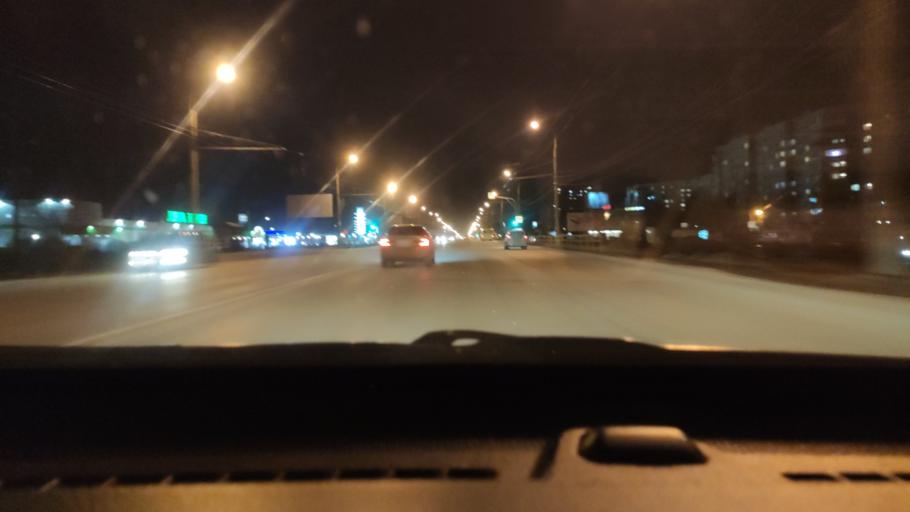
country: RU
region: Samara
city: Tol'yatti
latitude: 53.5505
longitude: 49.3378
